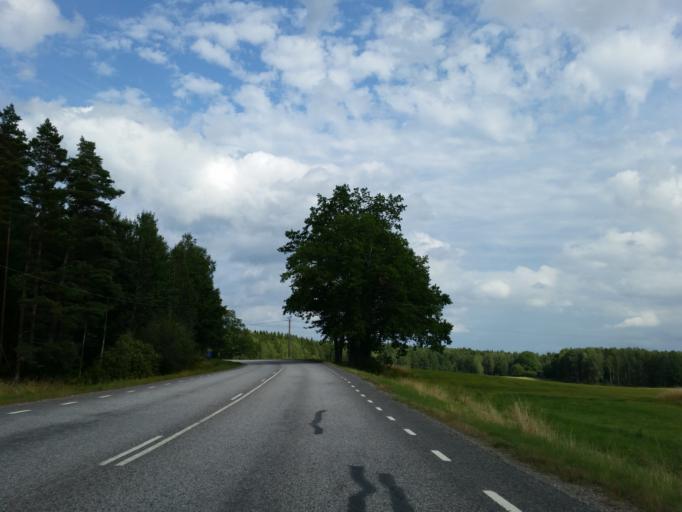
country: SE
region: Soedermanland
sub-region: Strangnas Kommun
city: Mariefred
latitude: 59.2191
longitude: 17.2422
